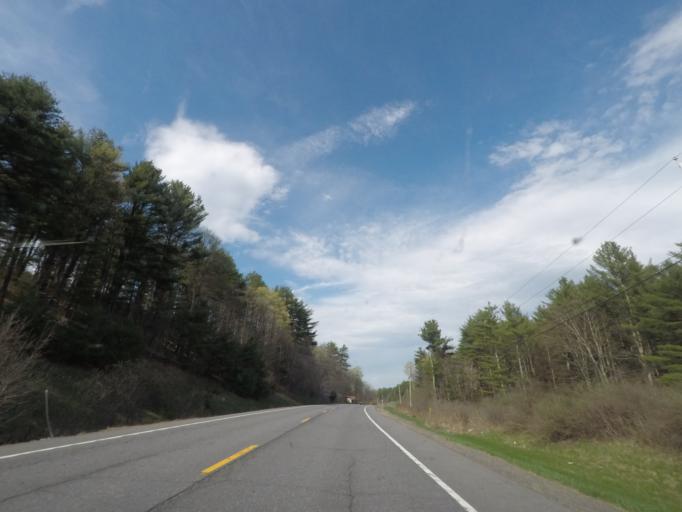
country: US
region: New York
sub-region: Albany County
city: Voorheesville
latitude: 42.5344
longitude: -73.9451
